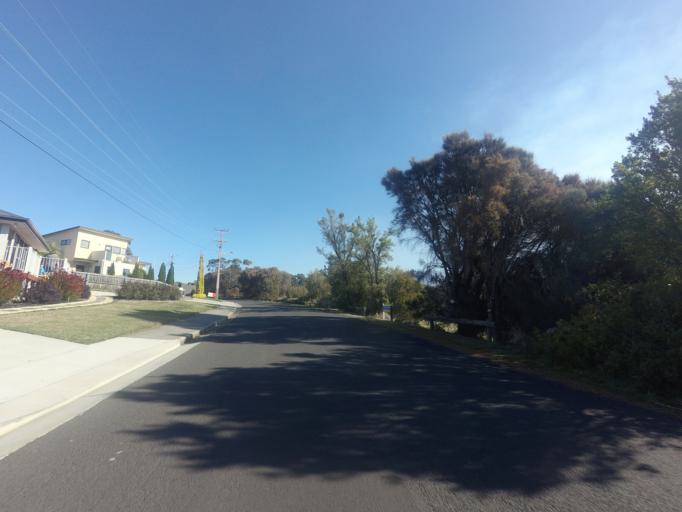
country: AU
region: Tasmania
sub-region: Clarence
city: Bellerive
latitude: -42.8708
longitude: 147.3530
